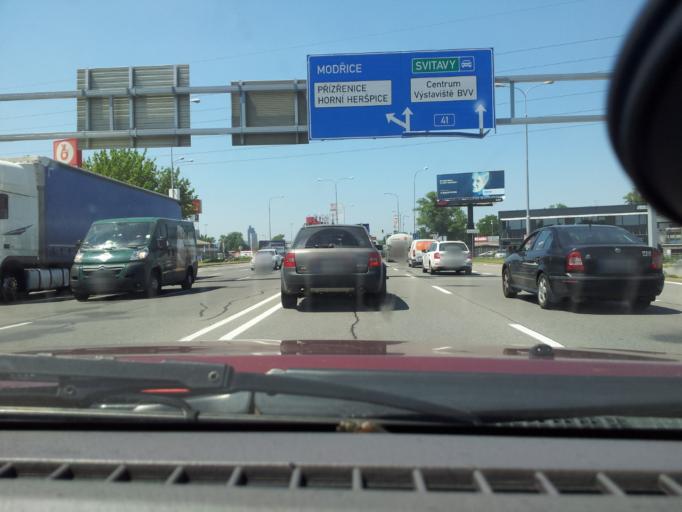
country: CZ
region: South Moravian
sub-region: Mesto Brno
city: Brno
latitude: 49.1659
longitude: 16.6301
